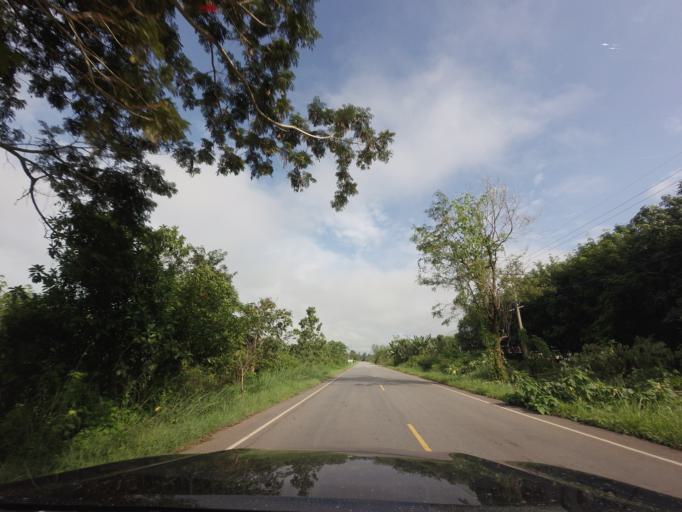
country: TH
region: Changwat Udon Thani
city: Nam Som
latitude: 17.8241
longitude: 102.2691
